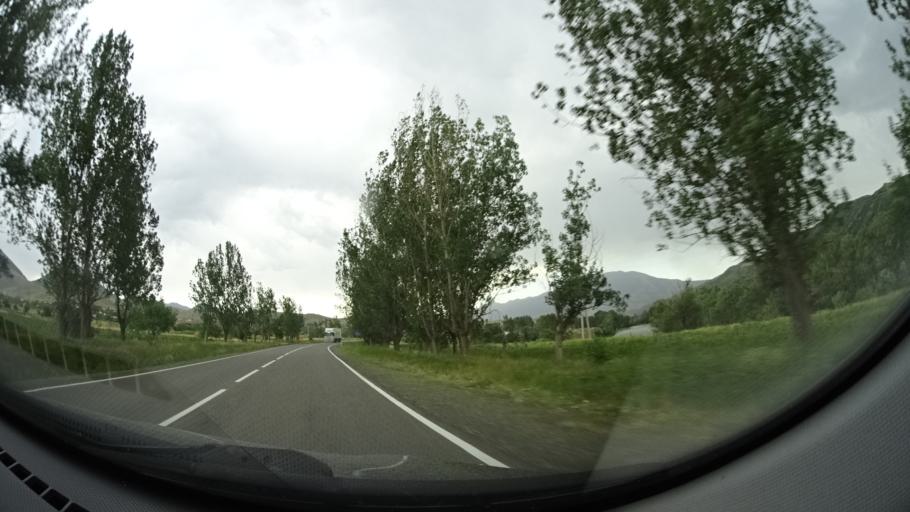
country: GE
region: Samtskhe-Javakheti
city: Akhaltsikhe
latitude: 41.6941
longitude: 43.0707
